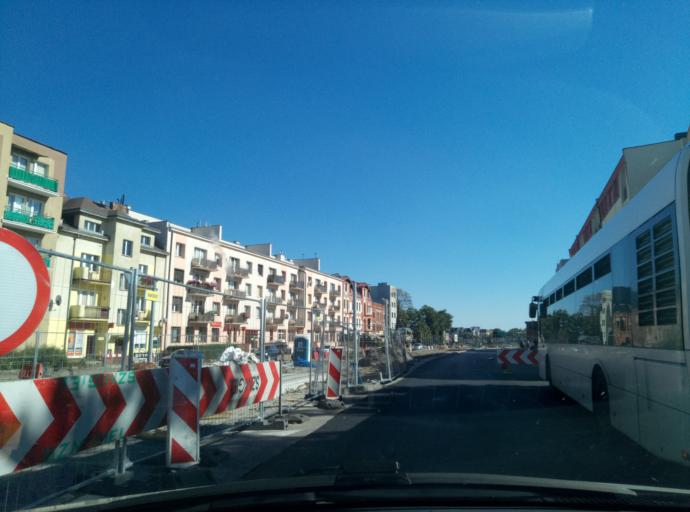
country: PL
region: Kujawsko-Pomorskie
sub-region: Torun
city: Torun
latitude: 53.0283
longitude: 18.5909
